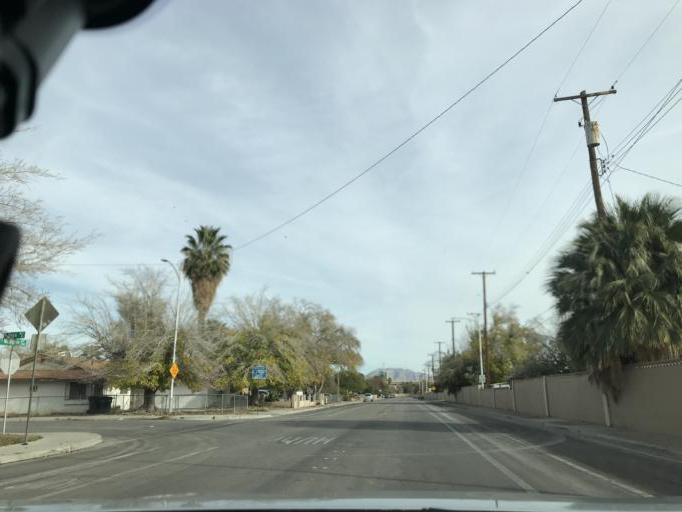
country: US
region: Nevada
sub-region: Clark County
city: Las Vegas
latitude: 36.1734
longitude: -115.1697
